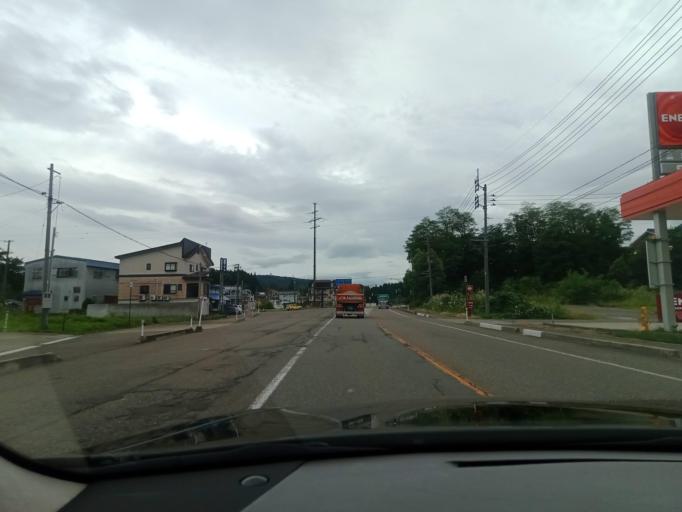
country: JP
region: Niigata
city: Arai
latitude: 36.8798
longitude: 138.2050
